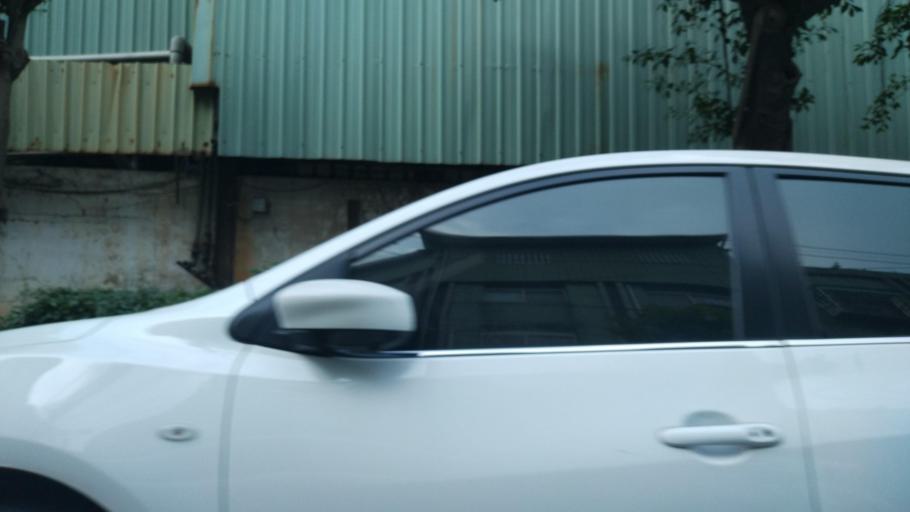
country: TW
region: Taipei
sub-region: Taipei
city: Banqiao
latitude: 24.9635
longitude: 121.4204
